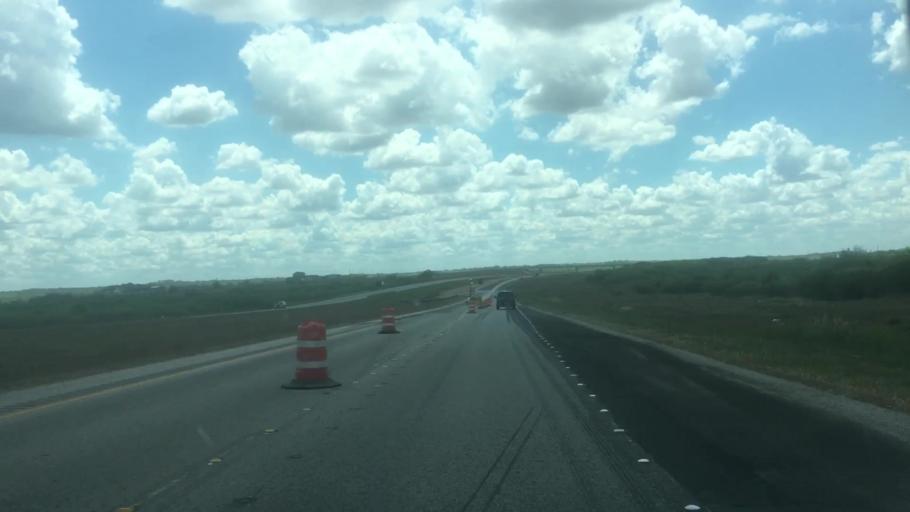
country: US
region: Texas
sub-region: Caldwell County
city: Lockhart
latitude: 29.8442
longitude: -97.7280
